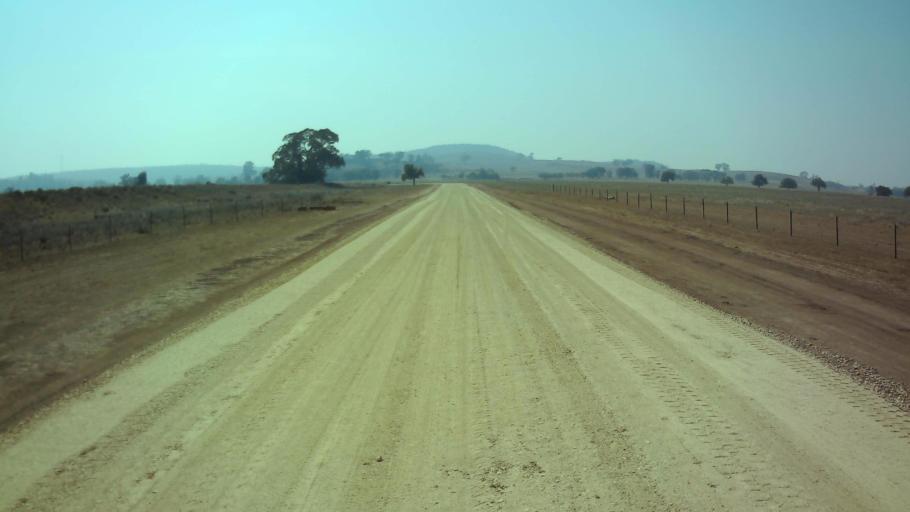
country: AU
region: New South Wales
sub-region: Weddin
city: Grenfell
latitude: -33.8564
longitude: 148.1085
